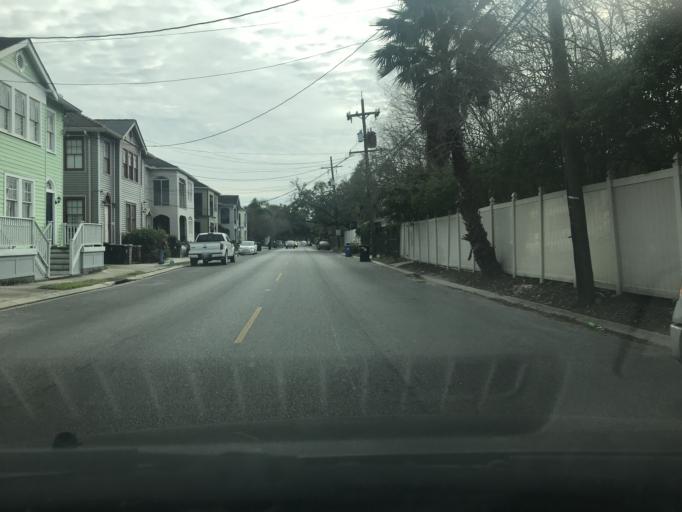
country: US
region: Louisiana
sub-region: Orleans Parish
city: New Orleans
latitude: 29.9524
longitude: -90.1077
